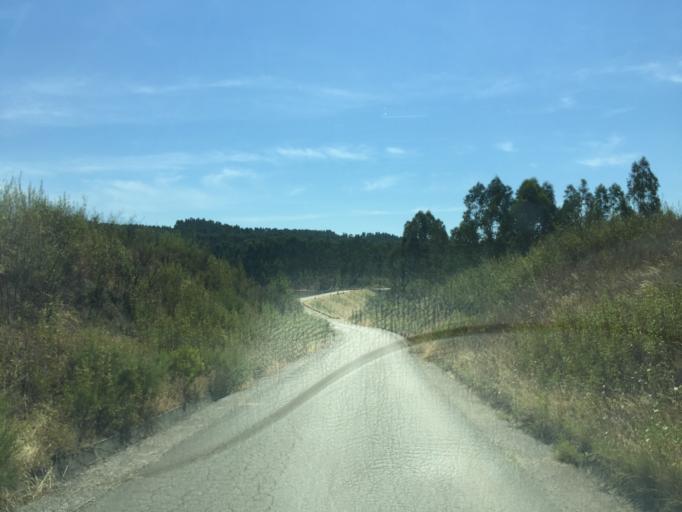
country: PT
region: Santarem
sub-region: Tomar
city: Tomar
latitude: 39.6097
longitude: -8.3606
